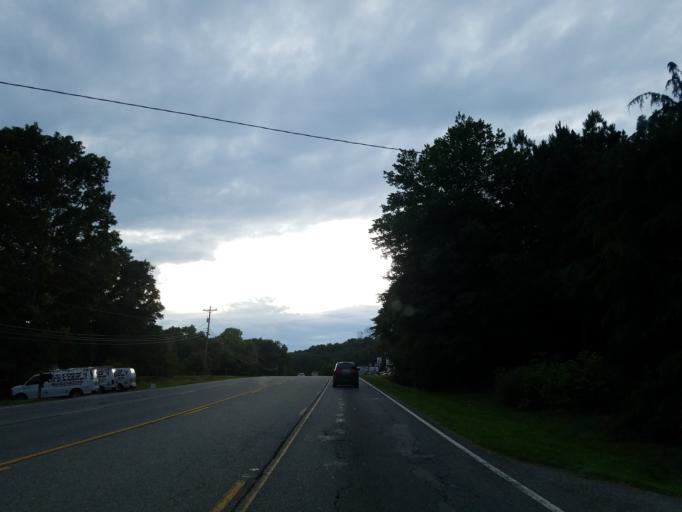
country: US
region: Georgia
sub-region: Forsyth County
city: Cumming
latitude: 34.2229
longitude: -84.1549
